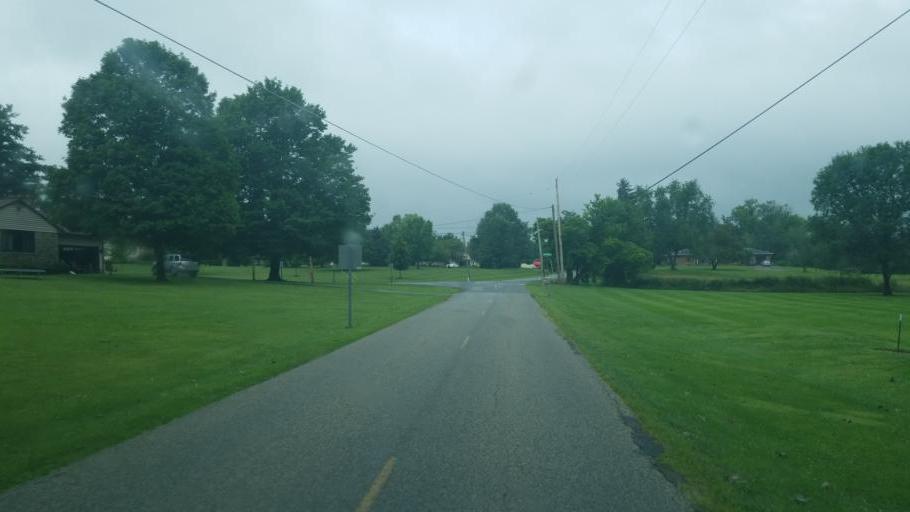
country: US
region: Ohio
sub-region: Delaware County
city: Sunbury
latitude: 40.2519
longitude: -82.8896
